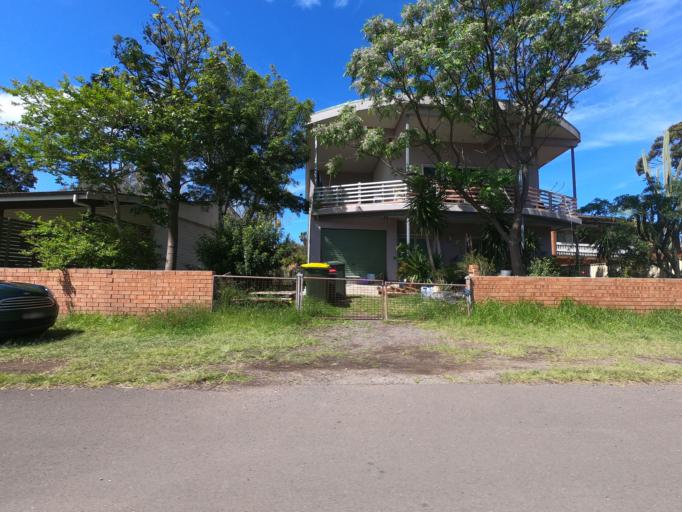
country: AU
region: New South Wales
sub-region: Wollongong
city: Lake Heights
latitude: -34.5012
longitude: 150.8737
